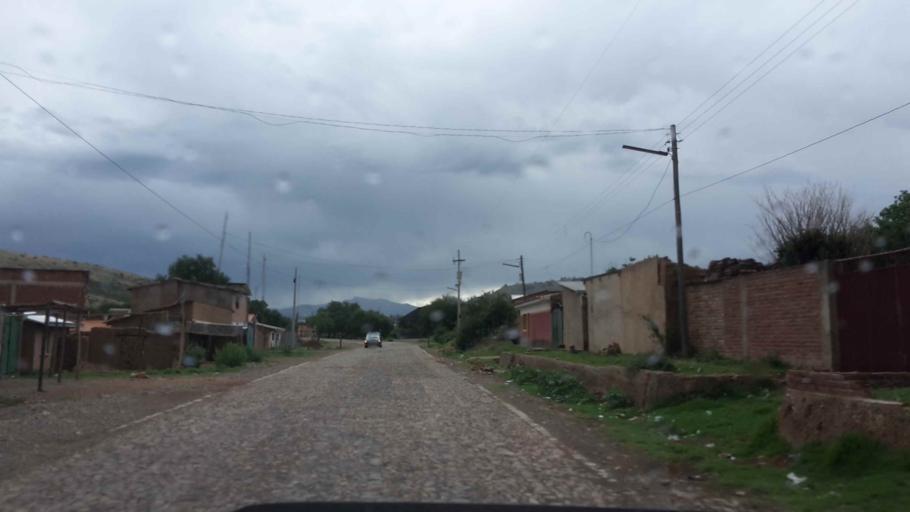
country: BO
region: Cochabamba
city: Cochabamba
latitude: -17.5489
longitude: -66.1779
